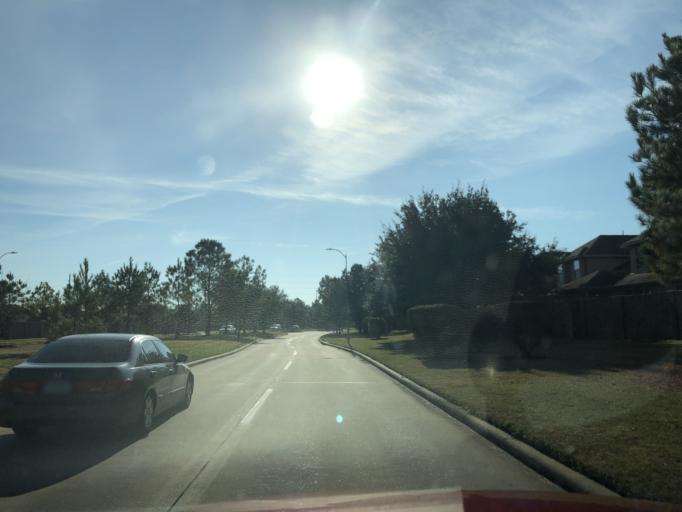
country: US
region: Texas
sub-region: Harris County
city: Tomball
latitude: 30.0491
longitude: -95.5653
